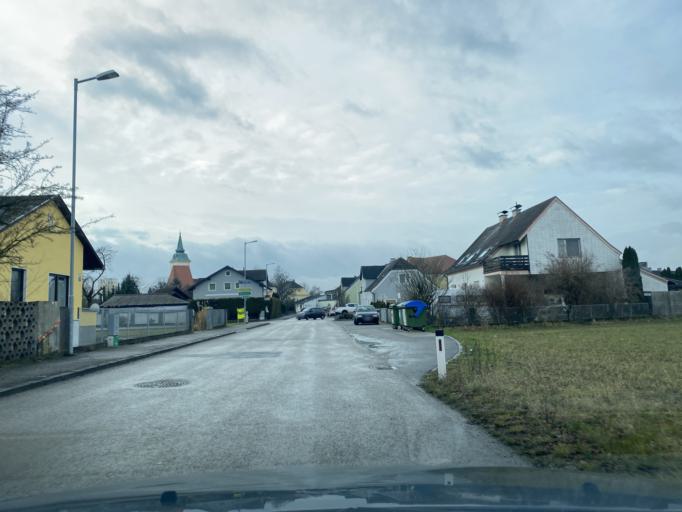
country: AT
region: Lower Austria
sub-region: Politischer Bezirk Sankt Polten
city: Prinzersdorf
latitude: 48.1946
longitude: 15.5036
